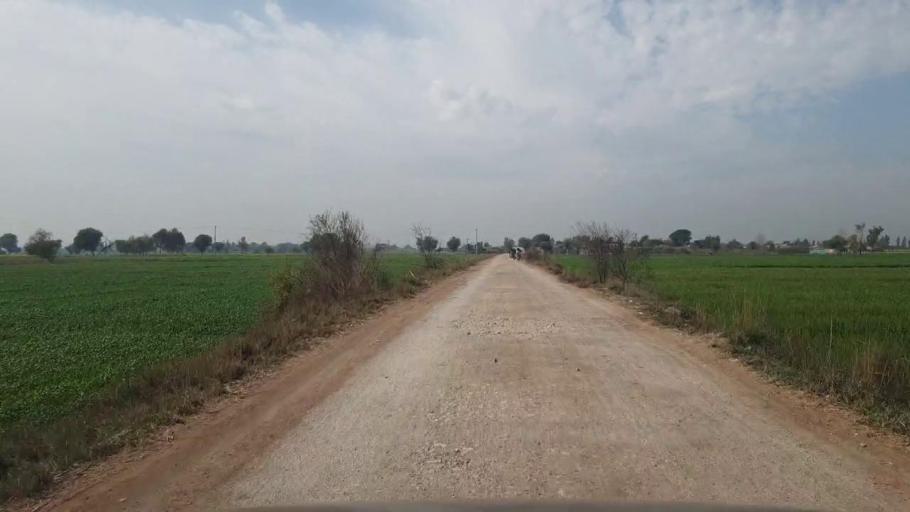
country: PK
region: Sindh
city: Sakrand
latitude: 25.9976
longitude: 68.3863
